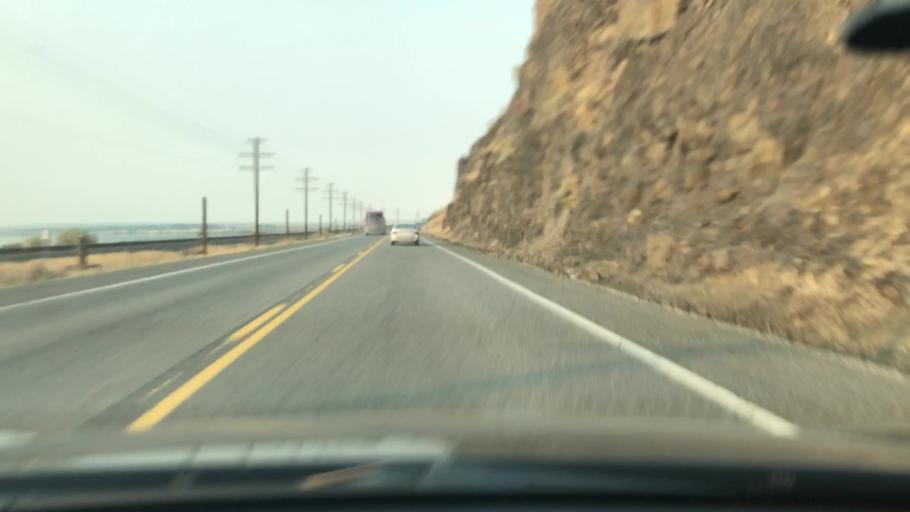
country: US
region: Washington
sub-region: Benton County
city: Finley
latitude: 46.0540
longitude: -118.9331
